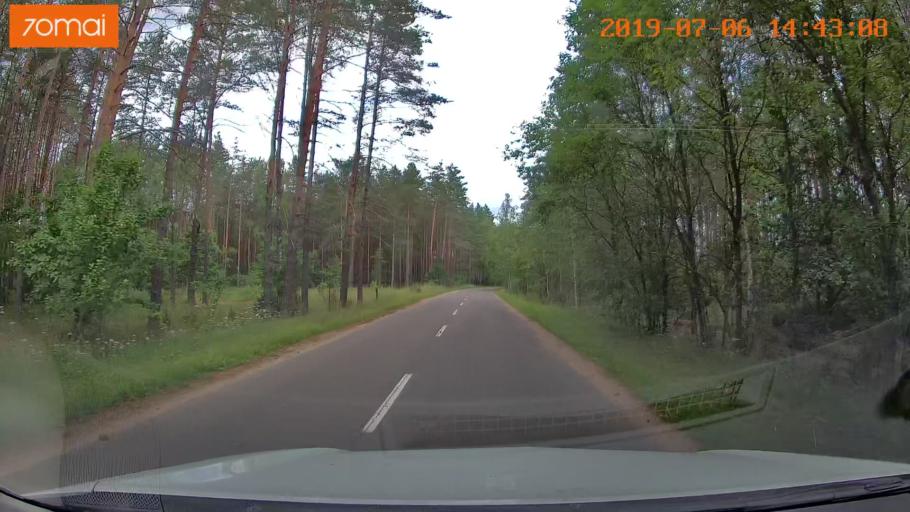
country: BY
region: Minsk
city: Ivyanyets
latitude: 53.9484
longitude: 26.6935
